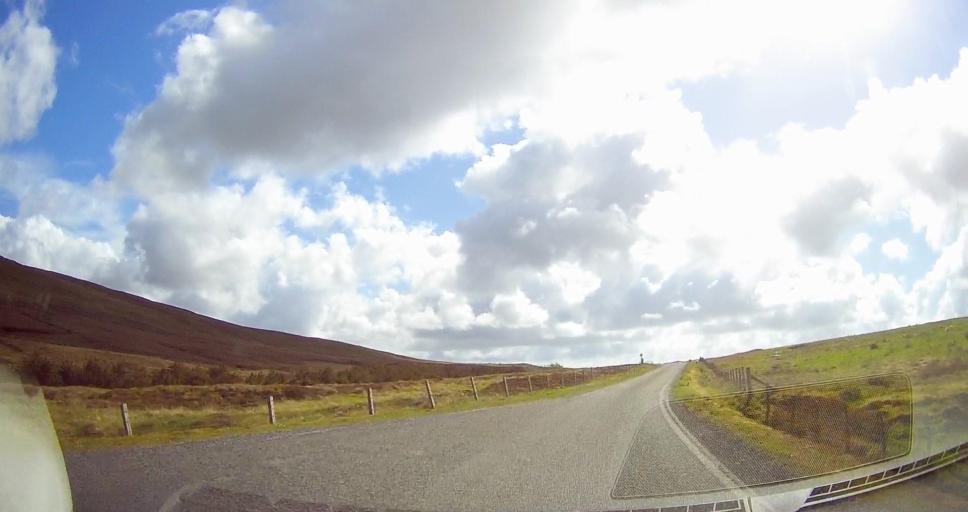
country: GB
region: Scotland
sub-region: Shetland Islands
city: Lerwick
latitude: 60.5082
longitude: -1.3870
